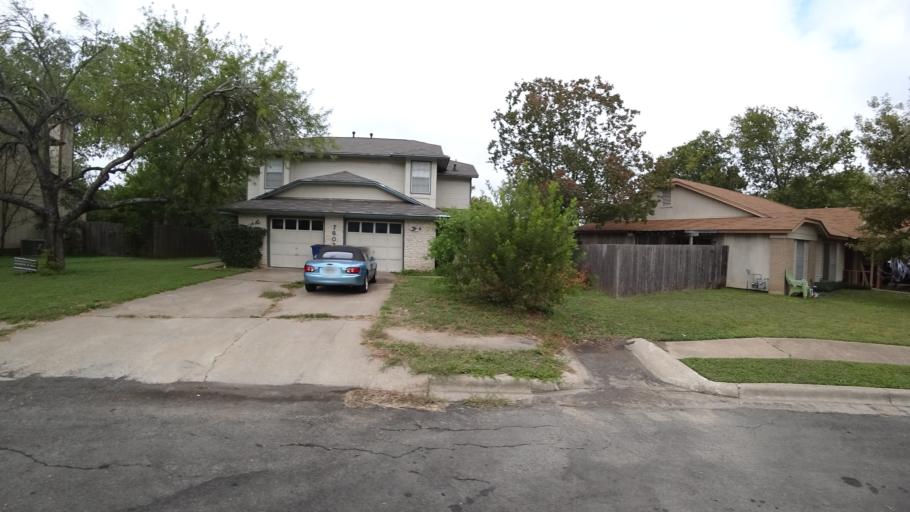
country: US
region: Texas
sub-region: Travis County
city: Shady Hollow
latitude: 30.2065
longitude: -97.8361
